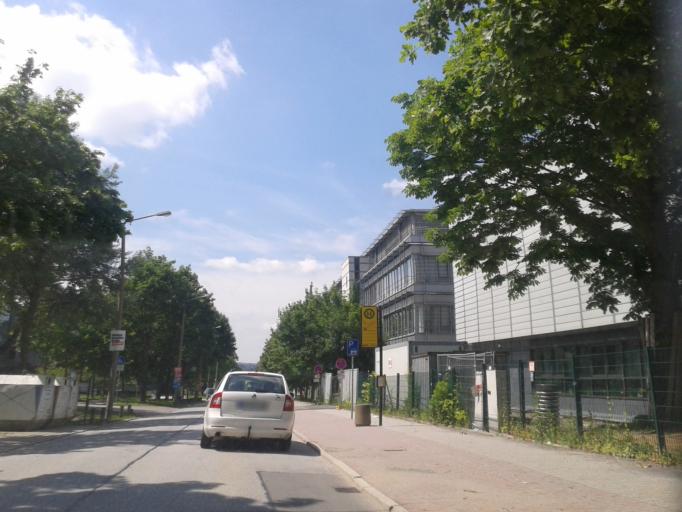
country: DE
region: Saxony
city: Dresden
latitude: 51.0256
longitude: 13.7253
